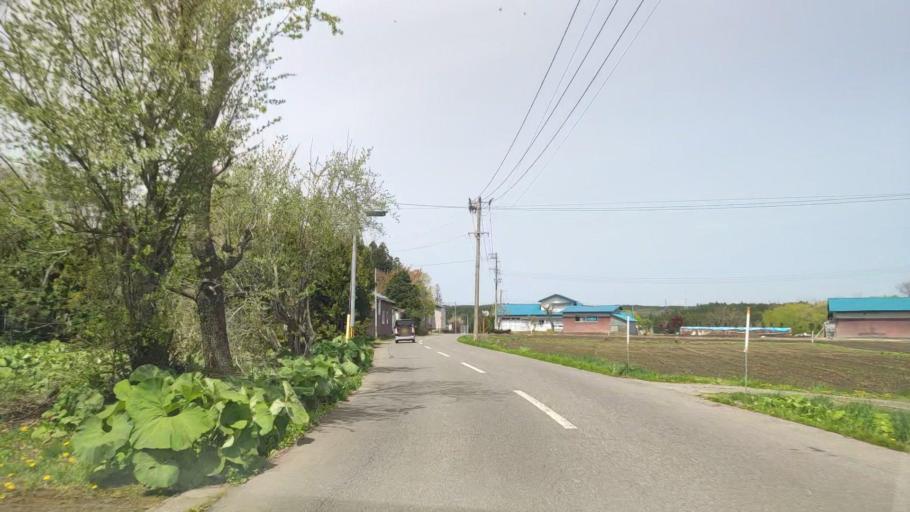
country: JP
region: Aomori
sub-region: Misawa Shi
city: Inuotose
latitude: 40.7751
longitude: 141.1215
